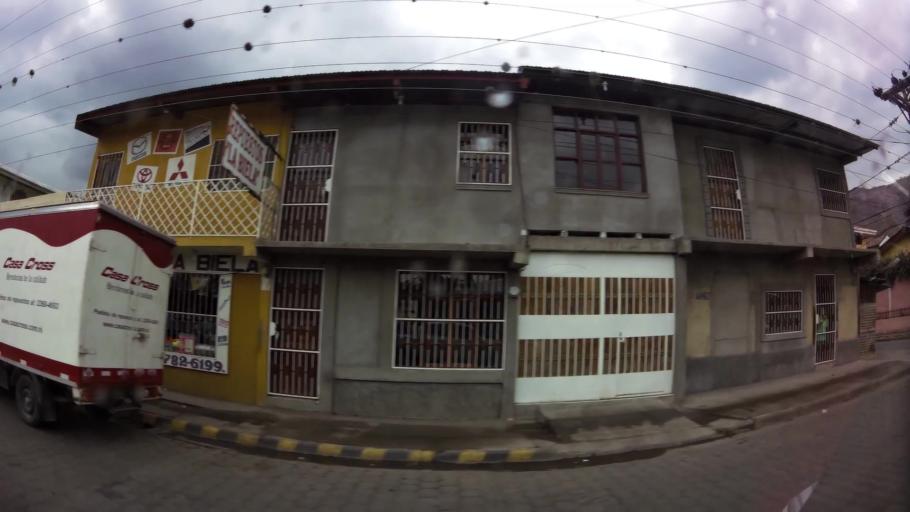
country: NI
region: Jinotega
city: Jinotega
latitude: 13.0914
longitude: -85.9993
